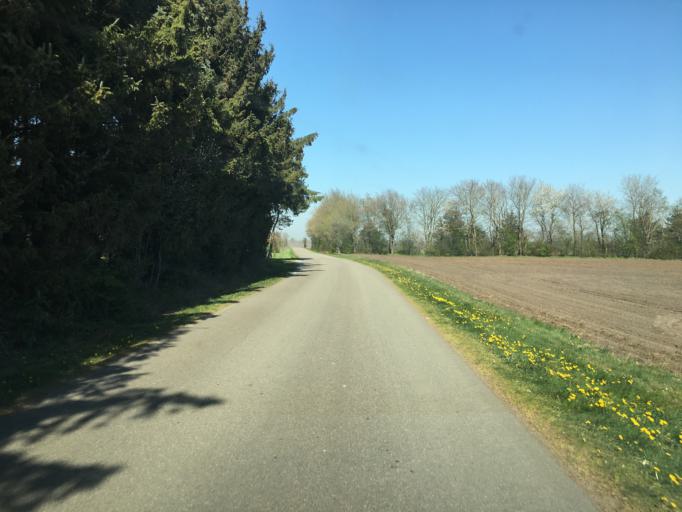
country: DK
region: South Denmark
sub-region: Aabenraa Kommune
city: Rodekro
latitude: 55.0772
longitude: 9.2562
